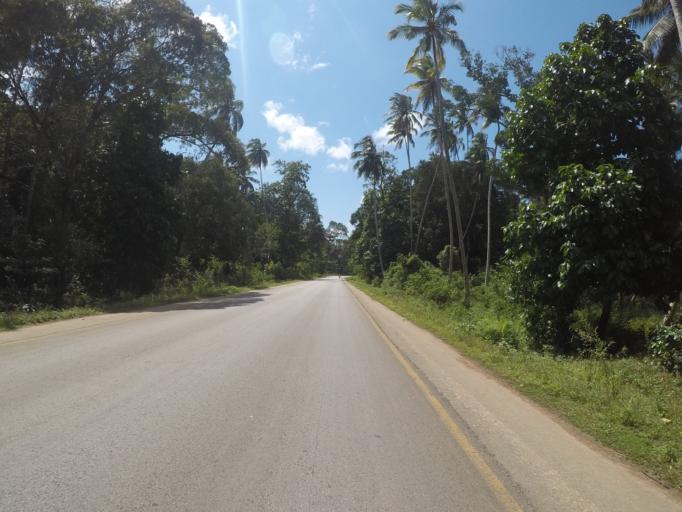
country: TZ
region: Zanzibar Central/South
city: Koani
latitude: -6.1459
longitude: 39.3284
